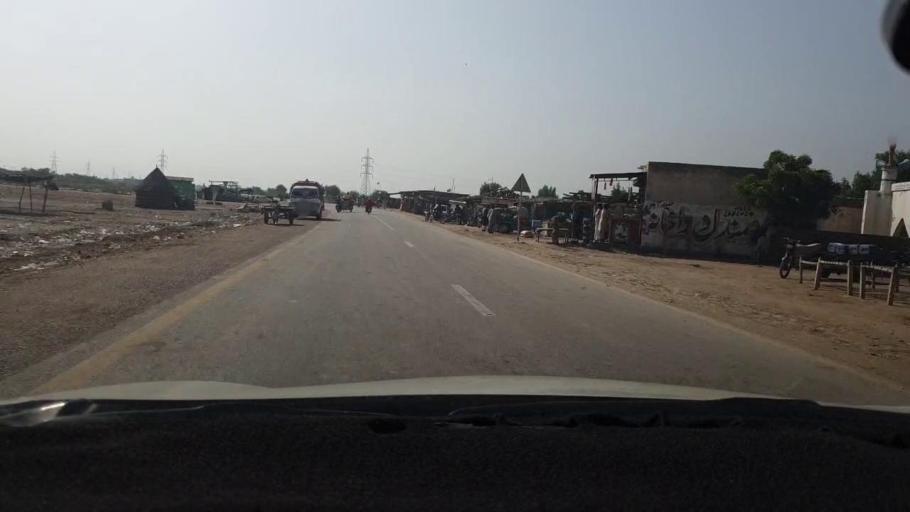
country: PK
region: Sindh
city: Jhol
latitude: 25.9280
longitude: 68.9980
